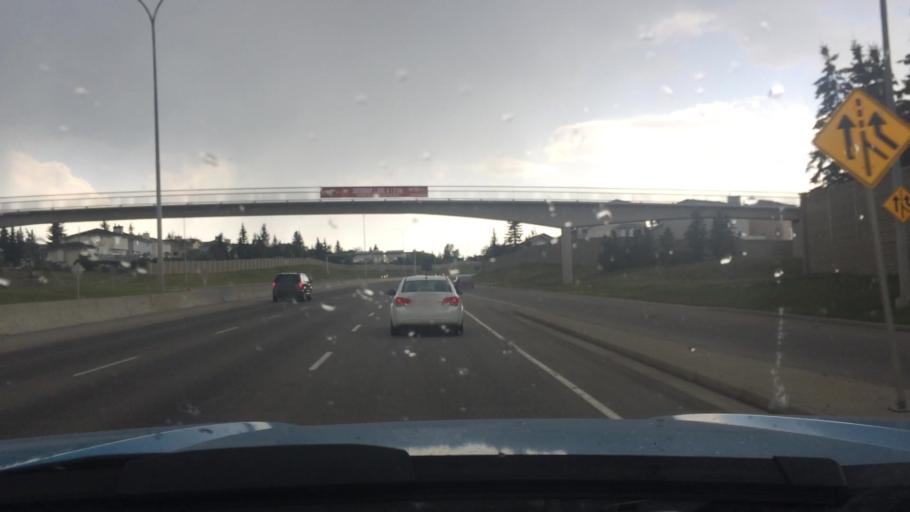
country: CA
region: Alberta
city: Calgary
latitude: 51.1435
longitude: -114.0951
